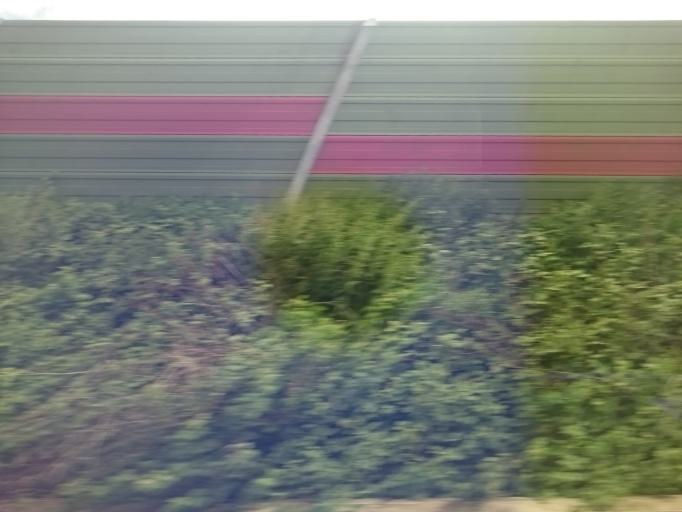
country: AT
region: Tyrol
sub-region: Politischer Bezirk Kufstein
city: Breitenbach am Inn
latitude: 47.4731
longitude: 11.9760
